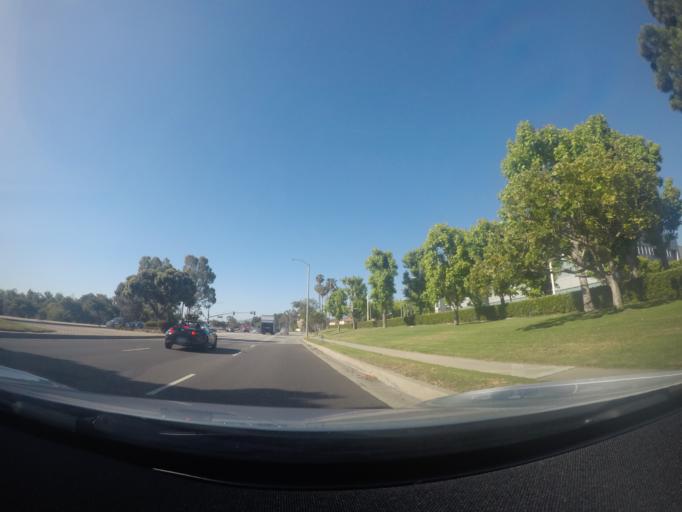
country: US
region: California
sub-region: Los Angeles County
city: Torrance
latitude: 33.8498
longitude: -118.3454
